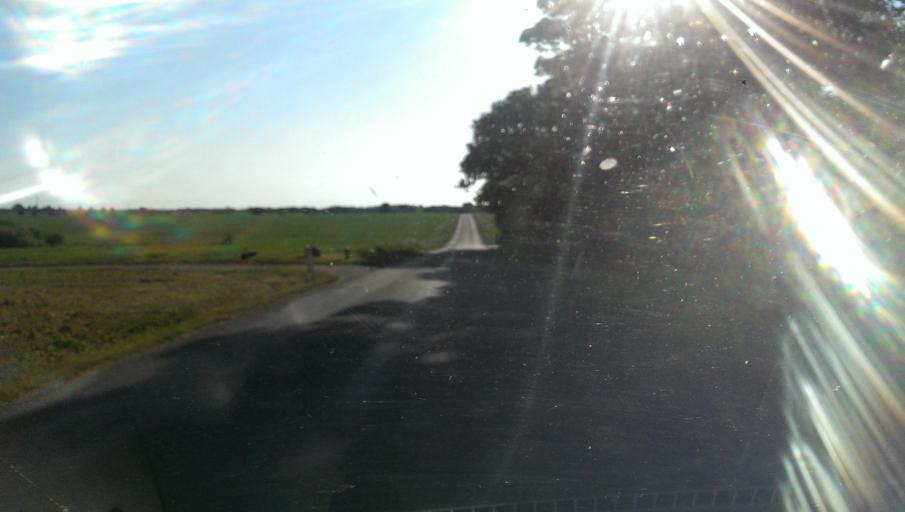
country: DK
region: South Denmark
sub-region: Esbjerg Kommune
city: Tjaereborg
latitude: 55.5138
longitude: 8.5841
